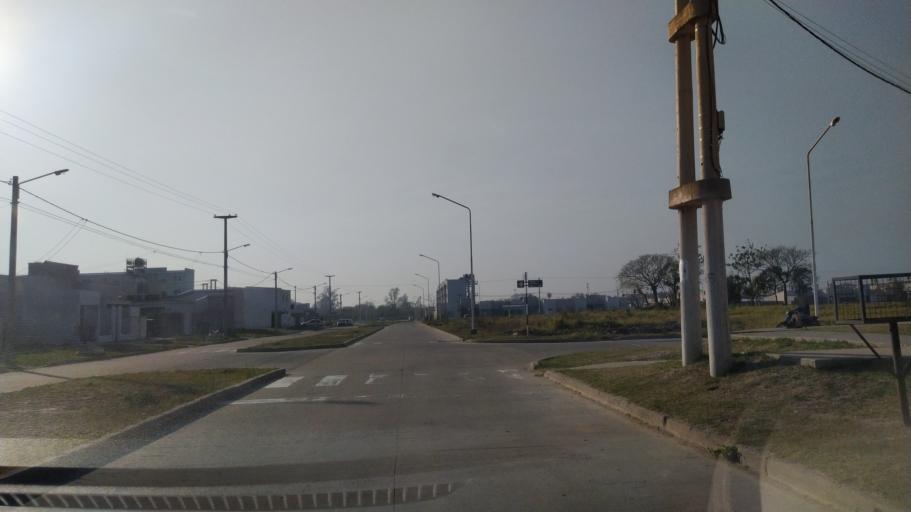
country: AR
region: Corrientes
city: Corrientes
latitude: -27.5240
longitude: -58.8046
